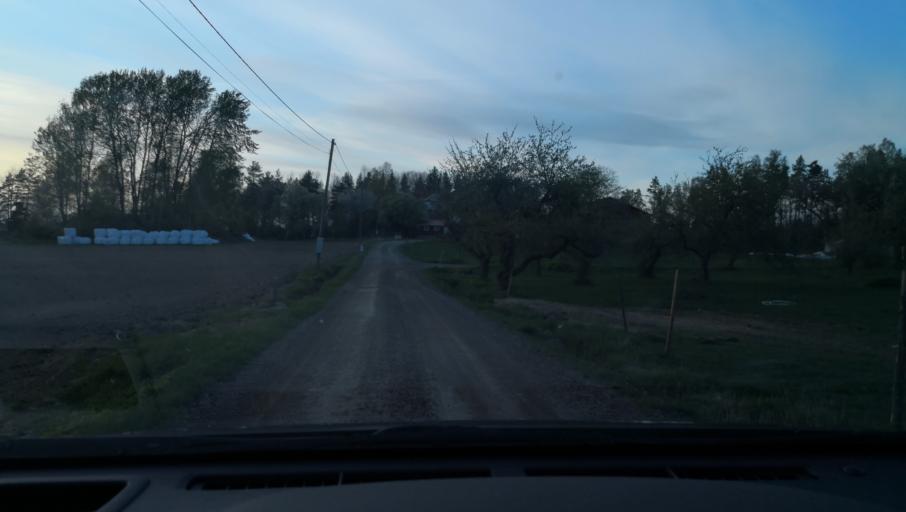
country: SE
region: OErebro
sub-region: Askersunds Kommun
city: Askersund
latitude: 58.9657
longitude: 14.9504
